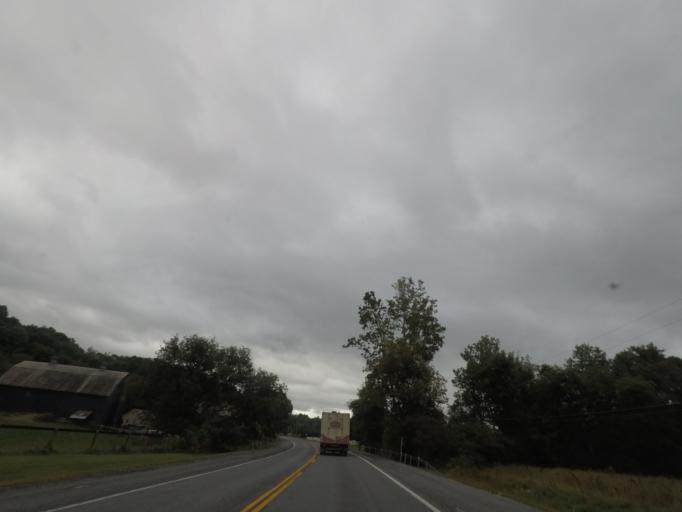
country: US
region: New York
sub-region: Rensselaer County
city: Hoosick Falls
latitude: 42.9335
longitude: -73.3621
